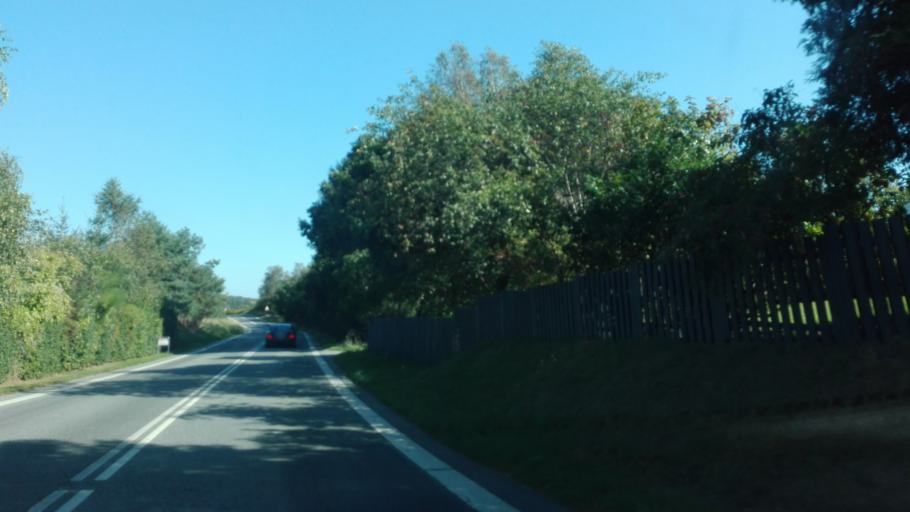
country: DK
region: Central Jutland
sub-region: Syddjurs Kommune
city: Ebeltoft
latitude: 56.2187
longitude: 10.6975
